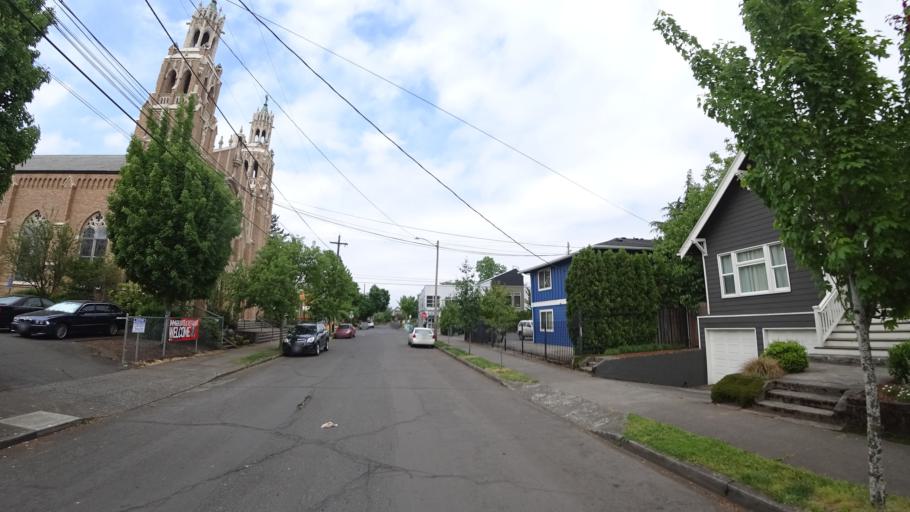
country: US
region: Oregon
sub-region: Multnomah County
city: Portland
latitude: 45.5586
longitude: -122.6566
